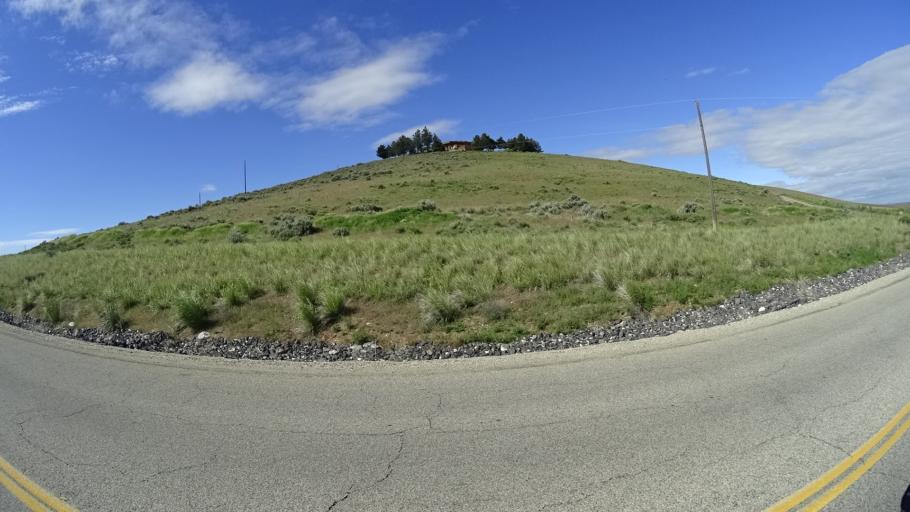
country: US
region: Idaho
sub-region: Ada County
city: Boise
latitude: 43.5114
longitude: -116.1486
